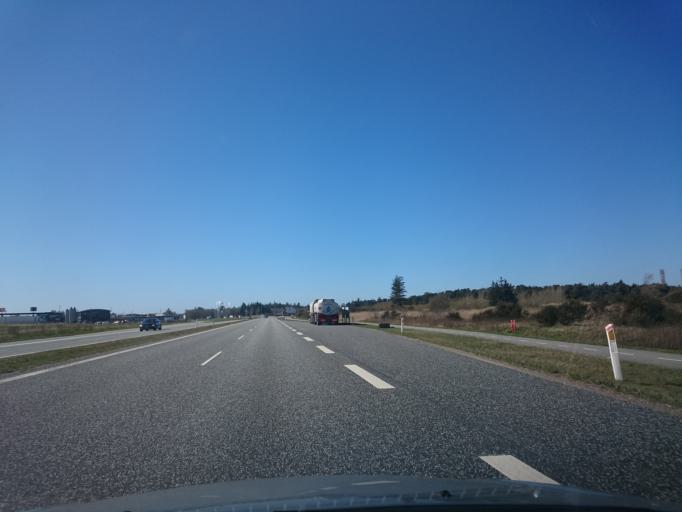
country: DK
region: North Denmark
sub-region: Hjorring Kommune
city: Hirtshals
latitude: 57.5755
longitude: 9.9929
